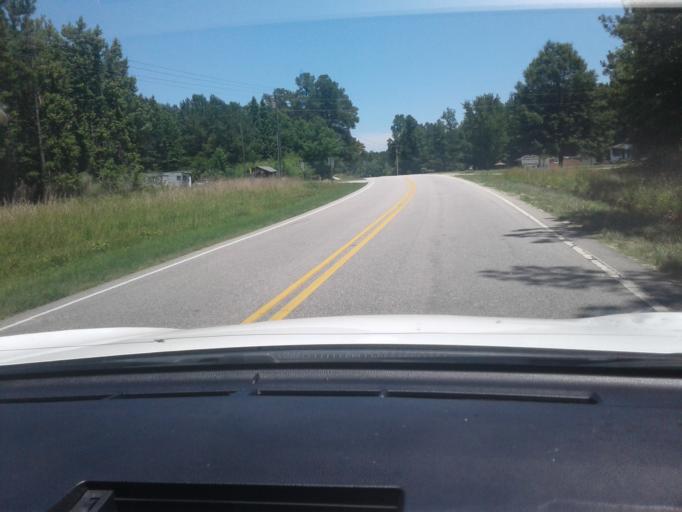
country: US
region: North Carolina
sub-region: Harnett County
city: Erwin
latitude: 35.3177
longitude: -78.7188
